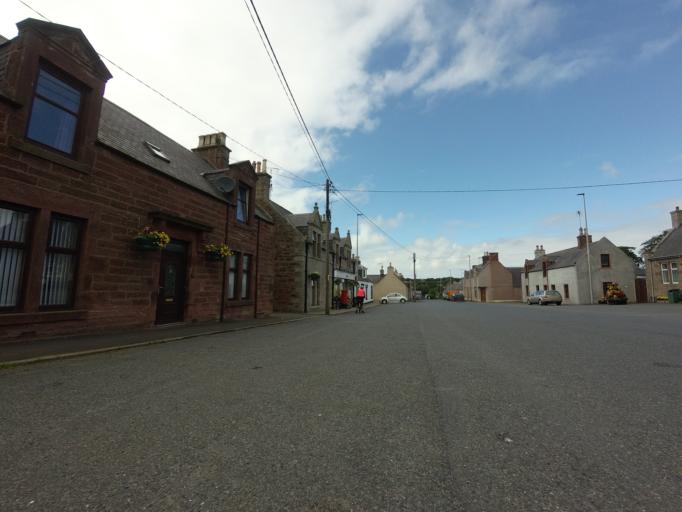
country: GB
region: Scotland
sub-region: Aberdeenshire
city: Turriff
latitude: 57.5423
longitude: -2.3351
